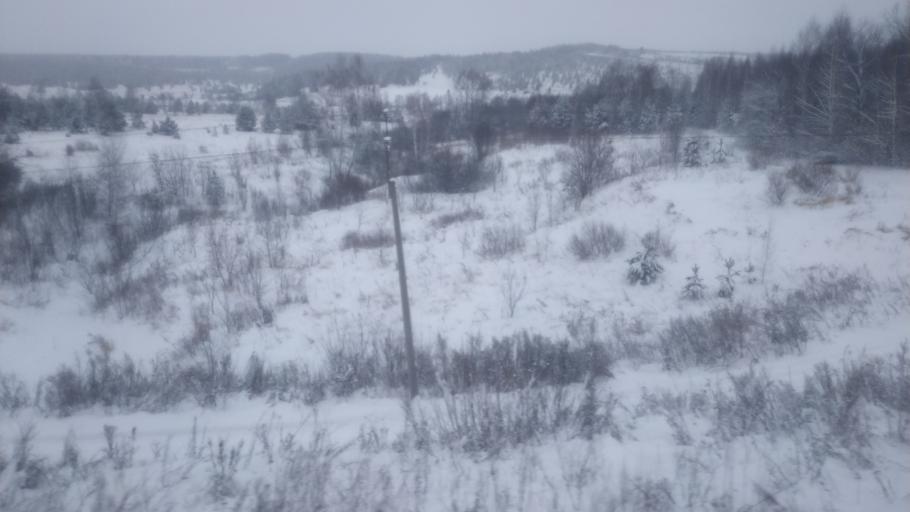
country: RU
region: Udmurtiya
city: Kiyasovo
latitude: 56.5015
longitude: 53.3663
